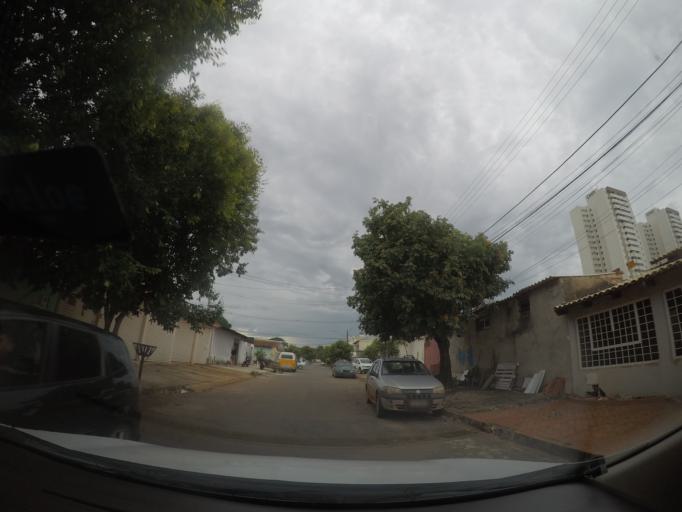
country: BR
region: Goias
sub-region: Goiania
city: Goiania
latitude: -16.6546
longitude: -49.2400
